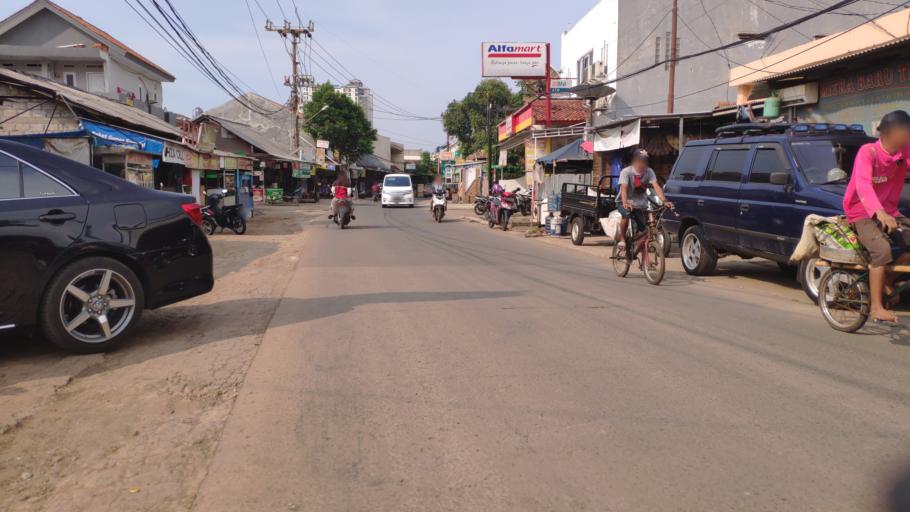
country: ID
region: West Java
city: Pamulang
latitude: -6.3414
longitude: 106.7927
